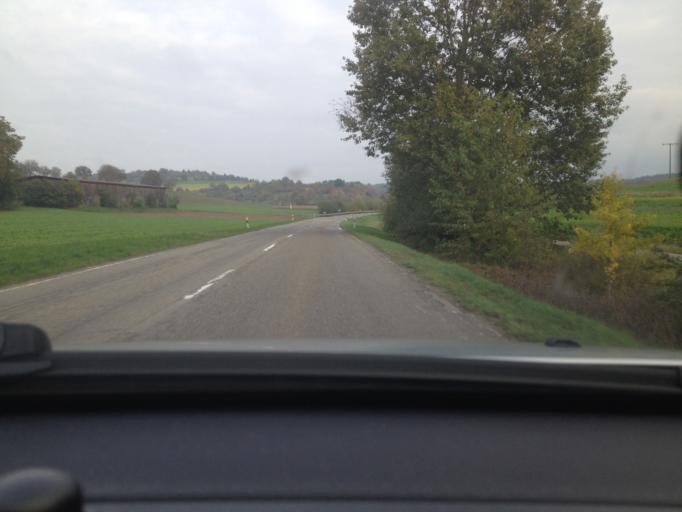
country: DE
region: Baden-Wuerttemberg
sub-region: Karlsruhe Region
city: Konigsbach-Stein
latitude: 48.9415
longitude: 8.5862
